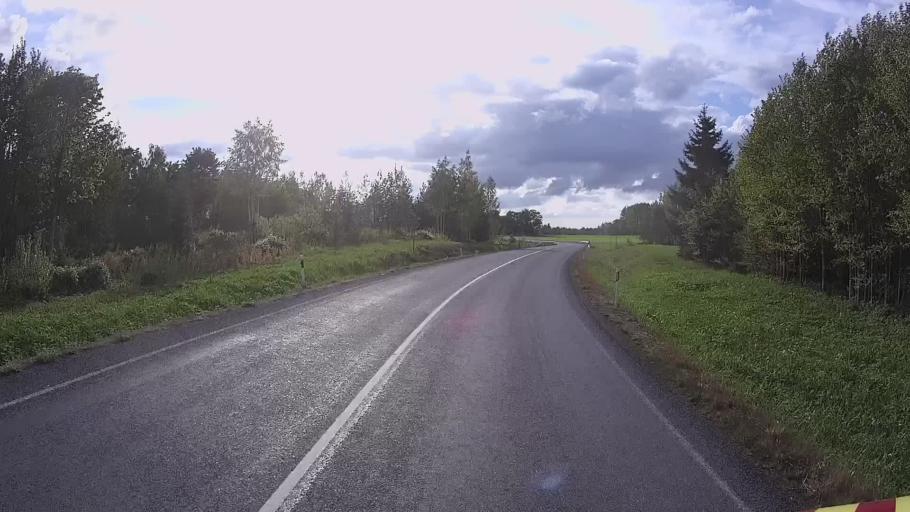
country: EE
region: Jogevamaa
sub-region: Mustvee linn
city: Mustvee
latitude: 59.0482
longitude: 27.0313
